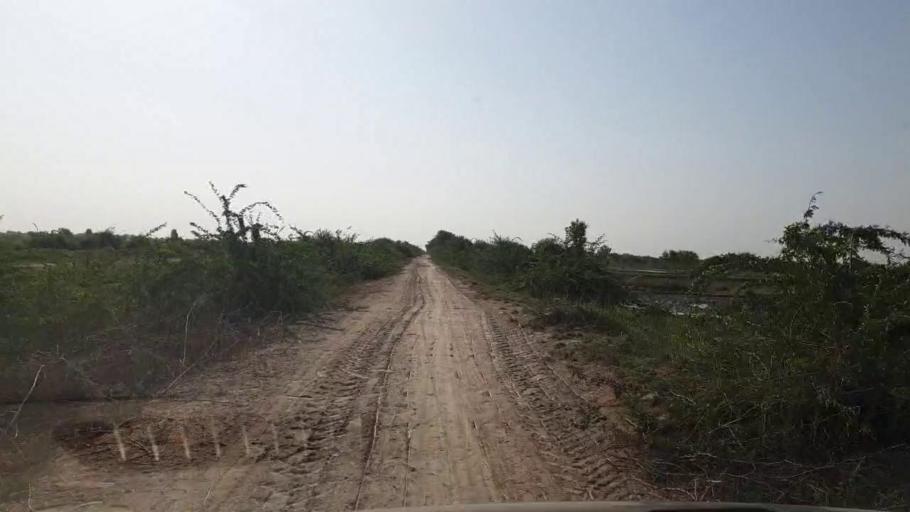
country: PK
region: Sindh
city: Kadhan
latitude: 24.5894
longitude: 69.0771
